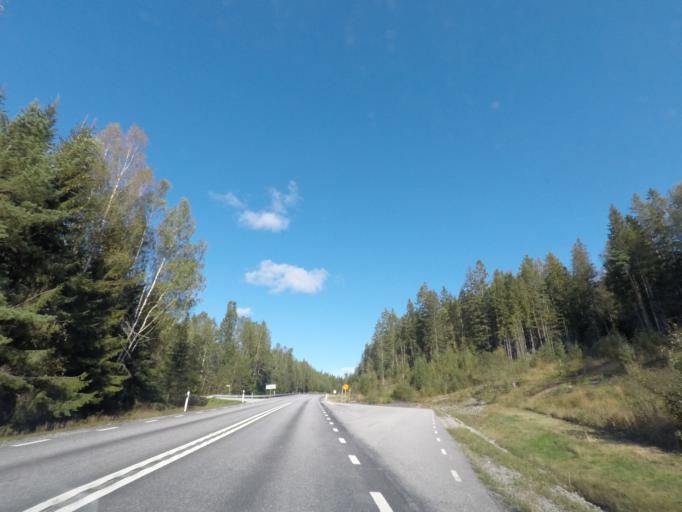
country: SE
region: Vaestmanland
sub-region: Skinnskattebergs Kommun
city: Skinnskatteberg
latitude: 59.8257
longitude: 15.5331
